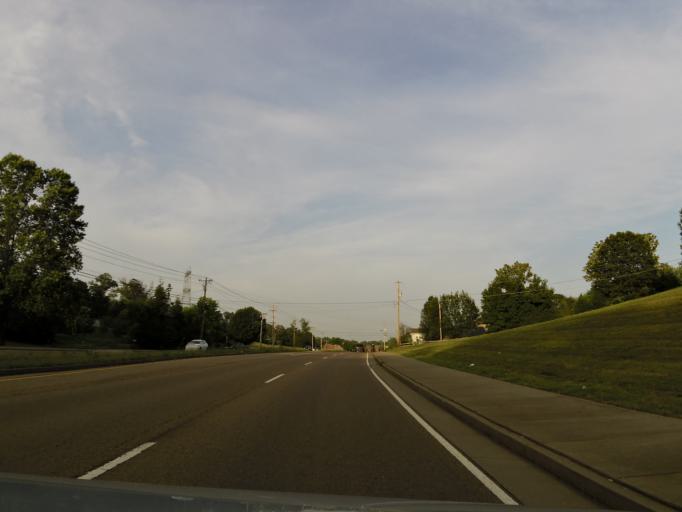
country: US
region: Tennessee
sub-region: Knox County
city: Farragut
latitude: 35.9457
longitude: -84.1046
